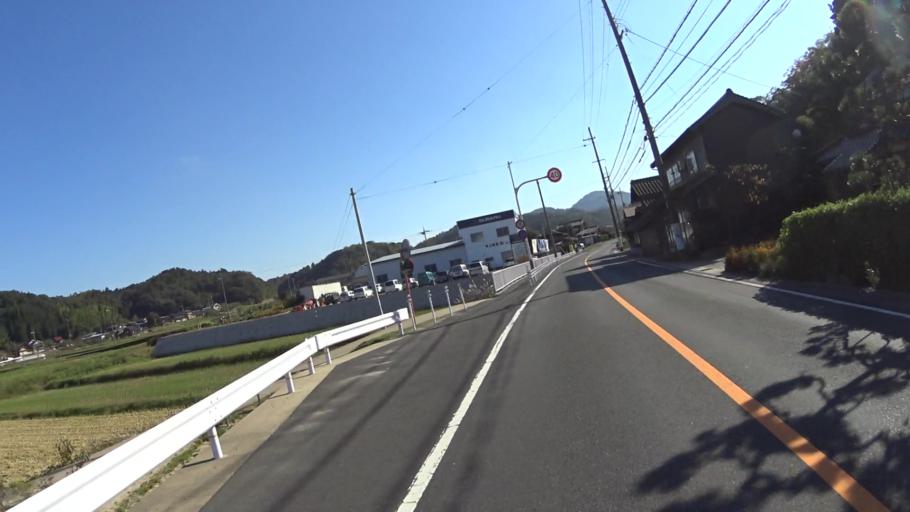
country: JP
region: Kyoto
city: Miyazu
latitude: 35.6571
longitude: 135.0321
